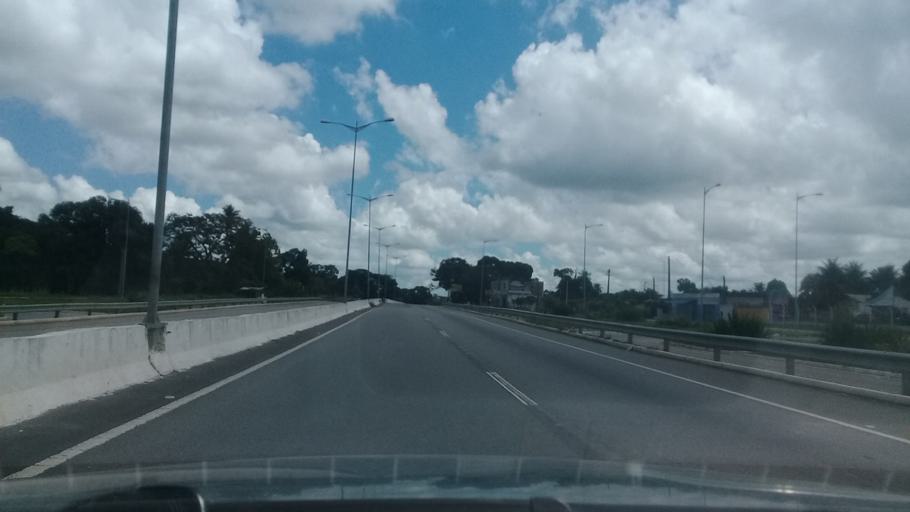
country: BR
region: Pernambuco
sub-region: Sao Lourenco Da Mata
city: Sao Lourenco da Mata
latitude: -7.9411
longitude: -35.1237
